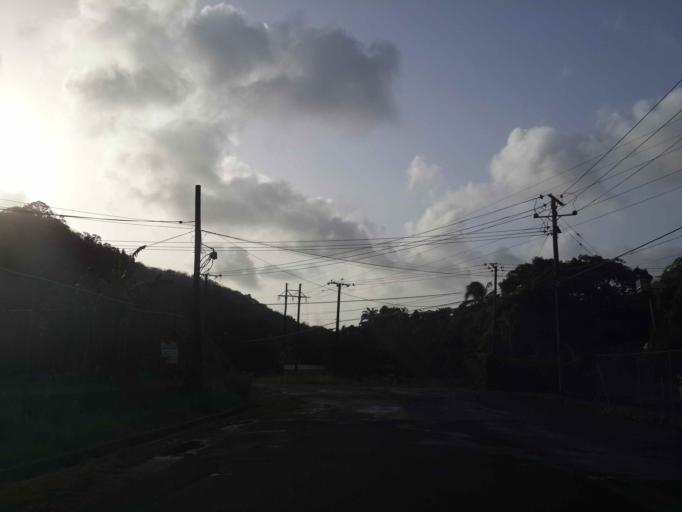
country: LC
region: Castries Quarter
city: Bisee
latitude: 14.0255
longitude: -60.9614
